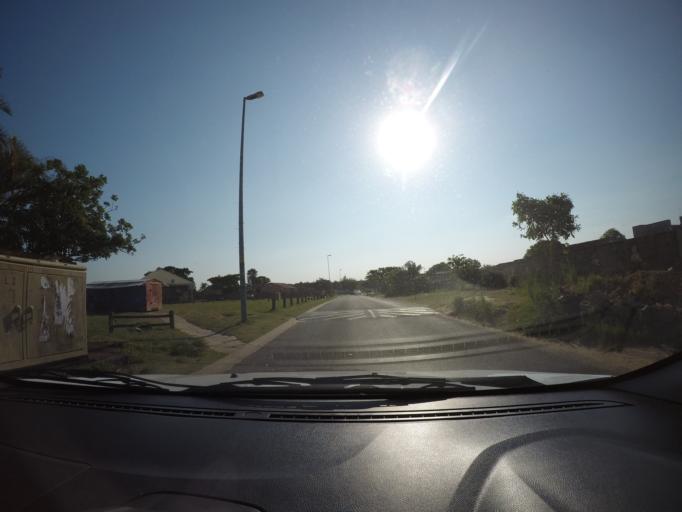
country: ZA
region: KwaZulu-Natal
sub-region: uThungulu District Municipality
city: Richards Bay
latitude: -28.7151
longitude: 32.0362
